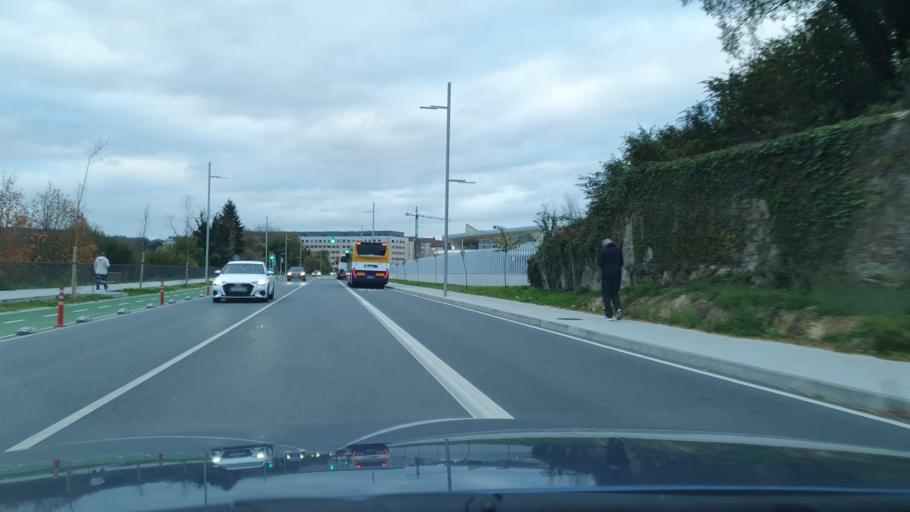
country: ES
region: Galicia
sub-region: Provincia da Coruna
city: Santiago de Compostela
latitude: 42.8711
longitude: -8.5413
